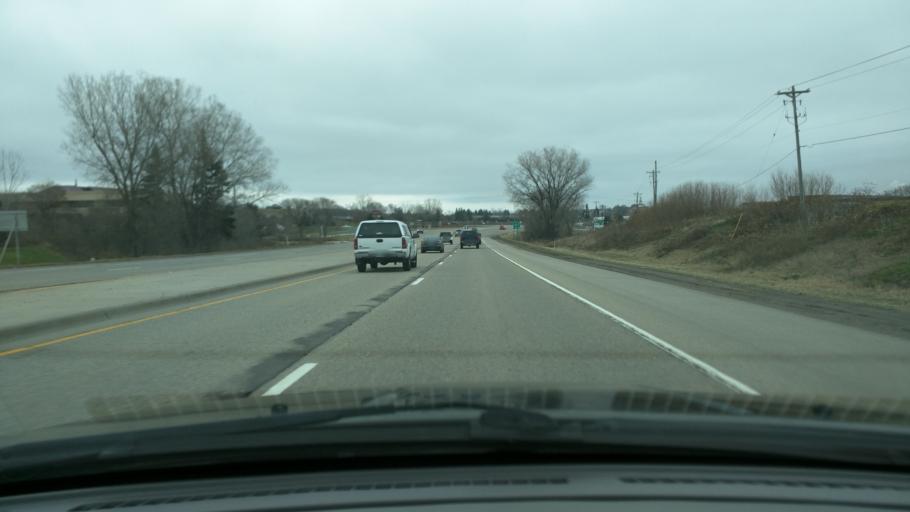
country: US
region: Minnesota
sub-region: Dakota County
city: Mendota Heights
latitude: 44.8547
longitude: -93.1351
